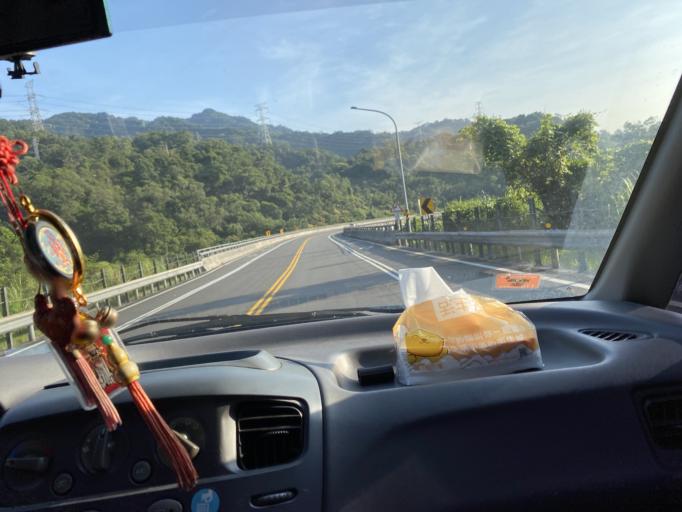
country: TW
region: Taiwan
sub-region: Keelung
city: Keelung
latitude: 25.0173
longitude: 121.8020
